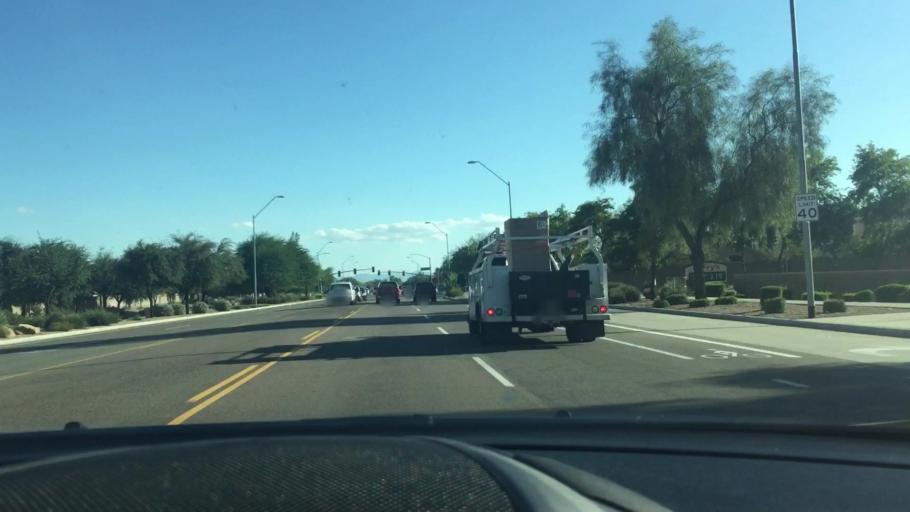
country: US
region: Arizona
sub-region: Maricopa County
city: Sun City
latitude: 33.6802
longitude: -112.2379
